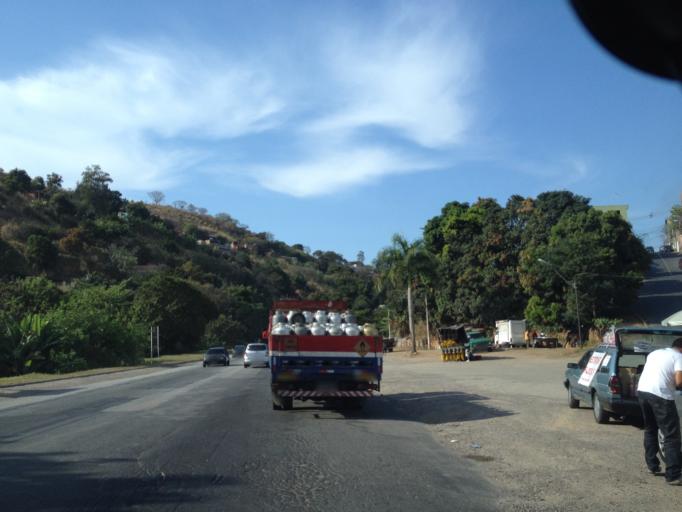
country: BR
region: Rio de Janeiro
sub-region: Volta Redonda
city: Volta Redonda
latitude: -22.5359
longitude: -44.1155
